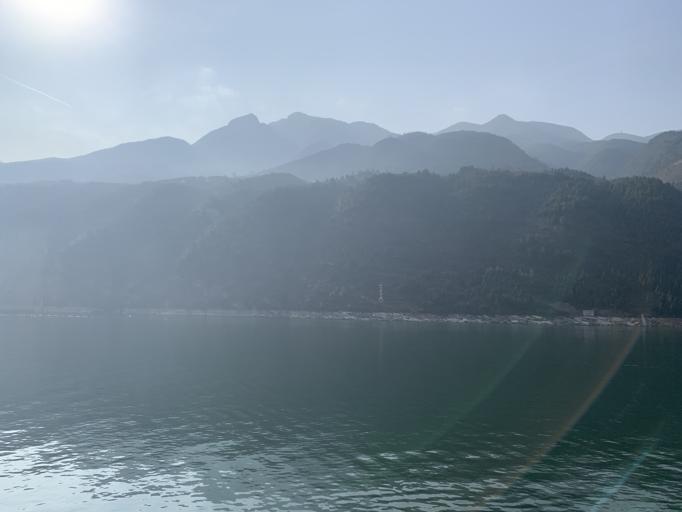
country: CN
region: Chongqing Shi
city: Baidi
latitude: 31.0418
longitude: 109.5707
